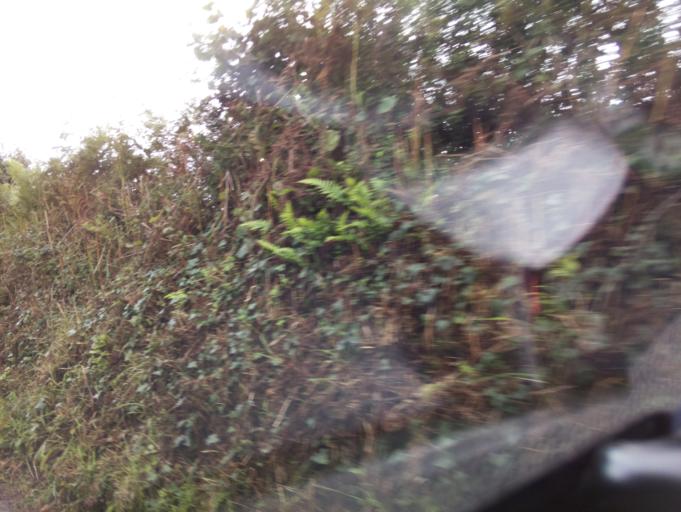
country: GB
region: England
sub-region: Devon
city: Dartmouth
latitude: 50.3307
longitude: -3.5880
